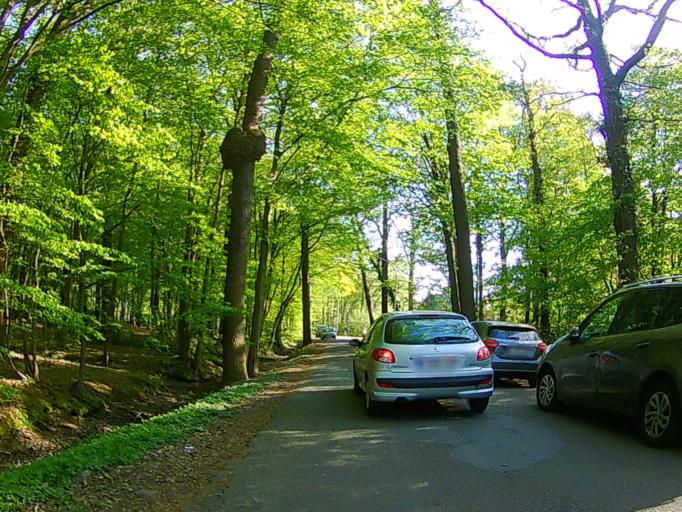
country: BE
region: Flanders
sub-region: Provincie Antwerpen
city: Schoten
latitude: 51.2459
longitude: 4.4839
